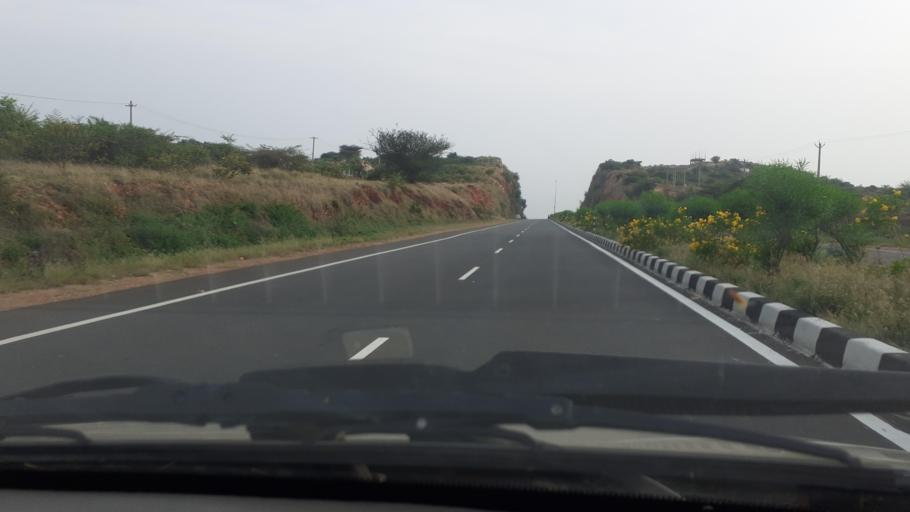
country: IN
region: Tamil Nadu
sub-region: Tirunelveli Kattabo
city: Tirunelveli
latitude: 8.6777
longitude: 77.7578
